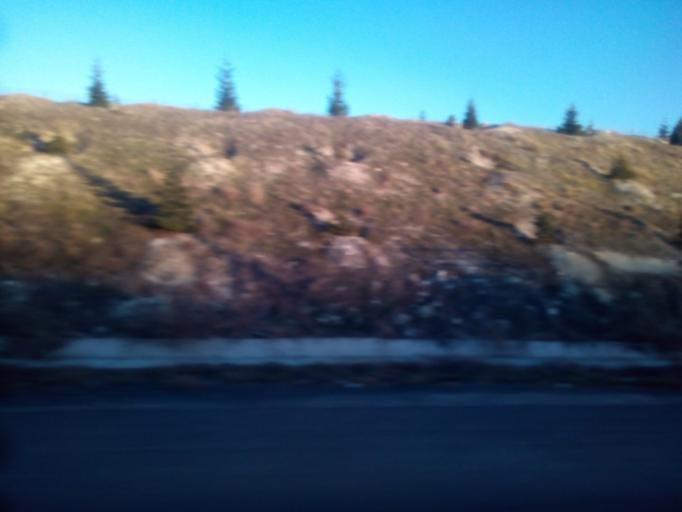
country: TR
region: Ankara
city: Etimesgut
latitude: 39.9076
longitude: 32.6277
